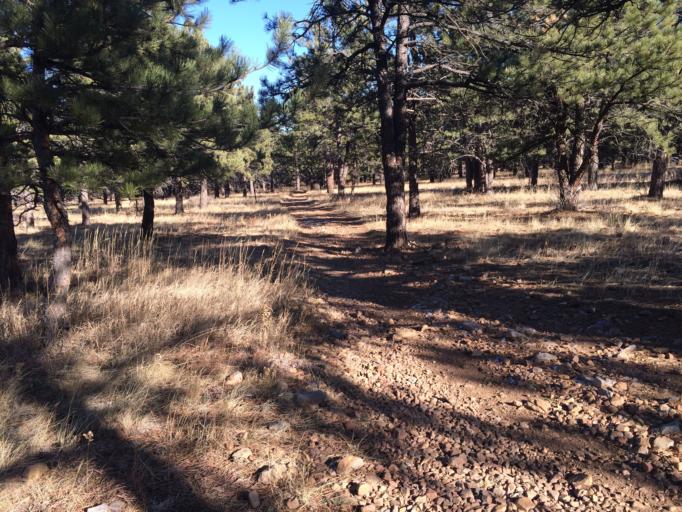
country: US
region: Colorado
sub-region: Boulder County
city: Superior
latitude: 39.9169
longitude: -105.2589
